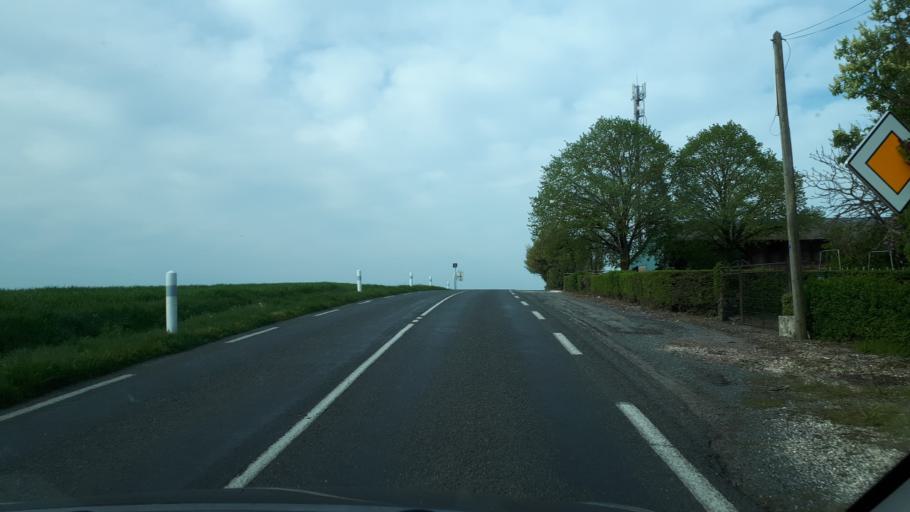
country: FR
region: Centre
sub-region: Departement du Cher
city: Rians
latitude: 47.2457
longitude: 2.6691
